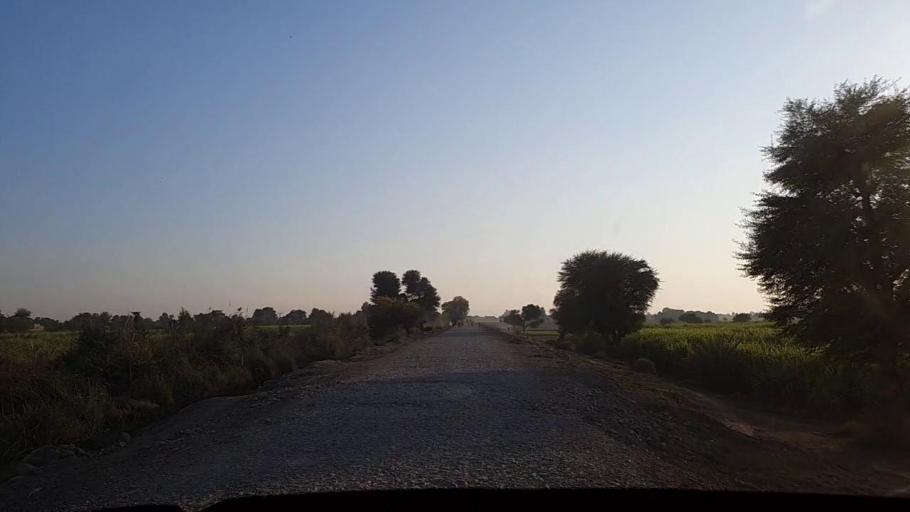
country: PK
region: Sindh
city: Sobhadero
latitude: 27.3718
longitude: 68.3782
